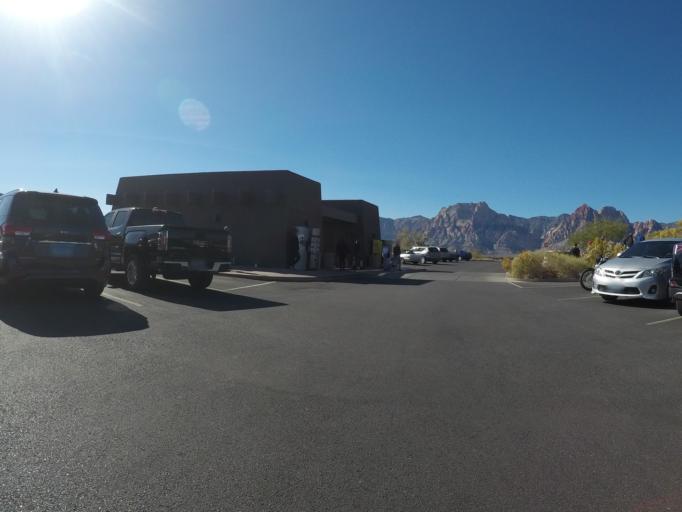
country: US
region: Nevada
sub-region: Clark County
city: Summerlin South
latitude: 36.1353
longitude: -115.4268
